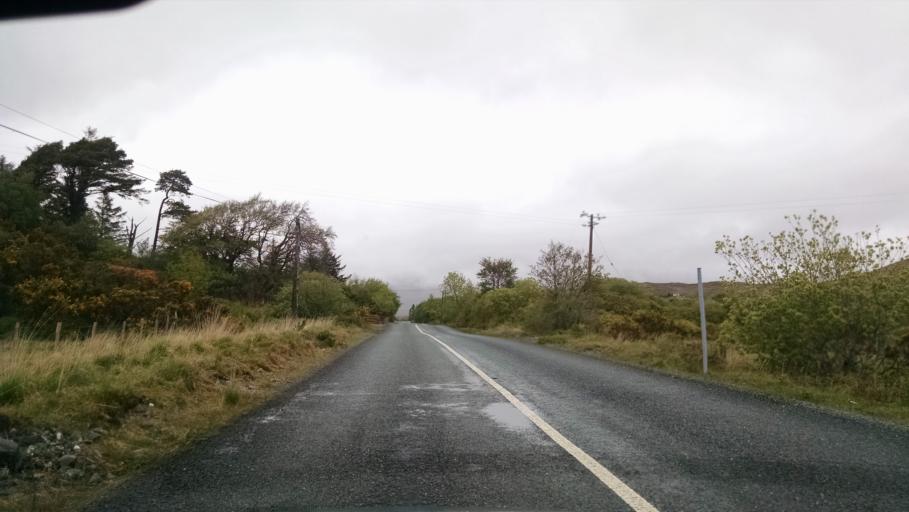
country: IE
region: Connaught
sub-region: County Galway
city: Clifden
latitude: 53.4823
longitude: -9.7411
